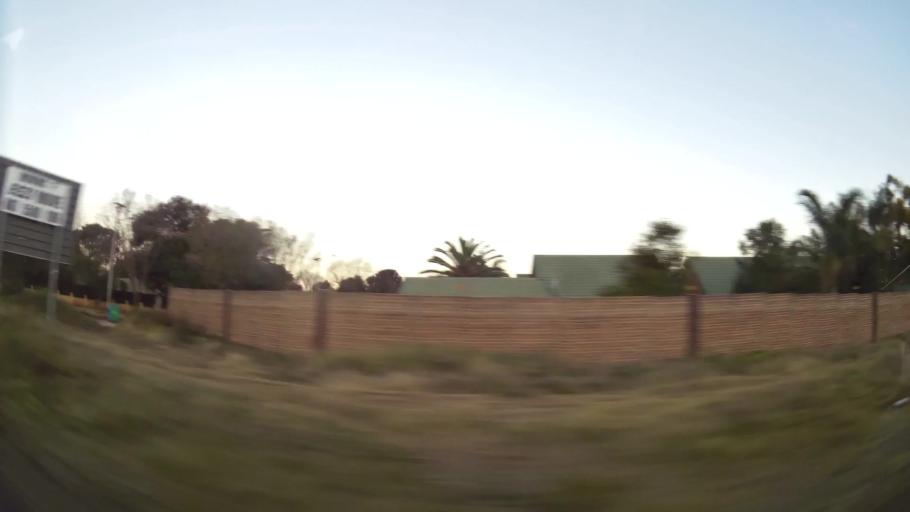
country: ZA
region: Gauteng
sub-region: City of Tshwane Metropolitan Municipality
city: Centurion
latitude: -25.8598
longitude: 28.1369
